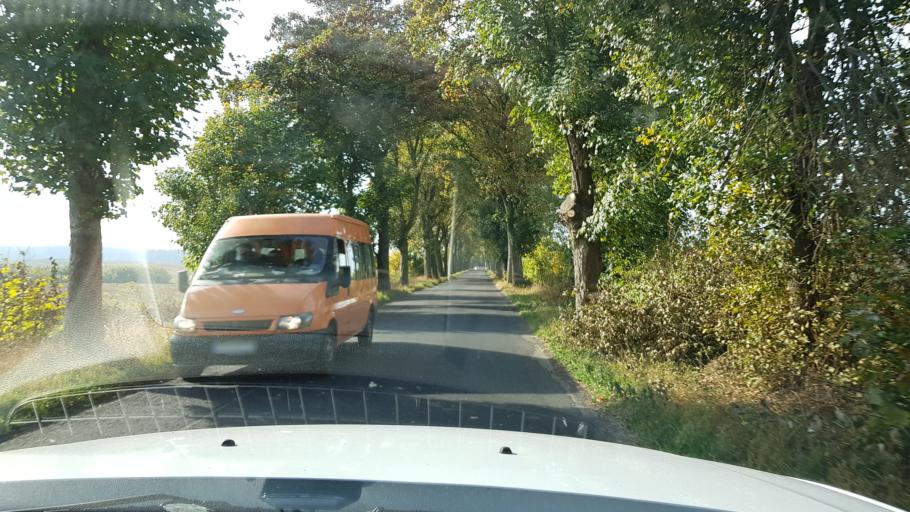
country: PL
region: West Pomeranian Voivodeship
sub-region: Powiat mysliborski
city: Nowogrodek Pomorski
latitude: 52.9573
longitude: 15.1088
